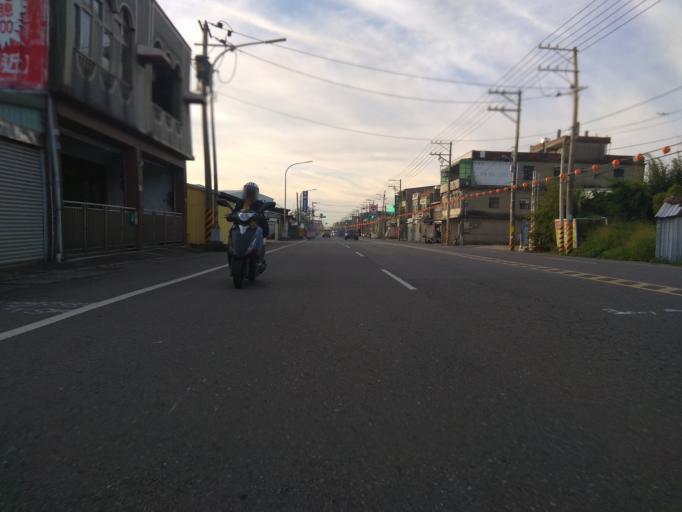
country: TW
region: Taiwan
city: Taoyuan City
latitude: 25.0012
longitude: 121.1553
